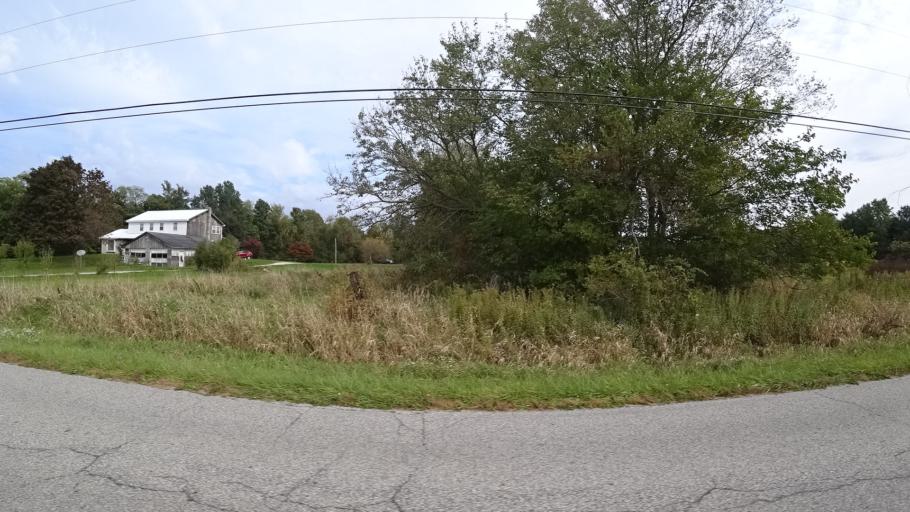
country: US
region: Indiana
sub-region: LaPorte County
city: Trail Creek
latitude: 41.7080
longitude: -86.8163
